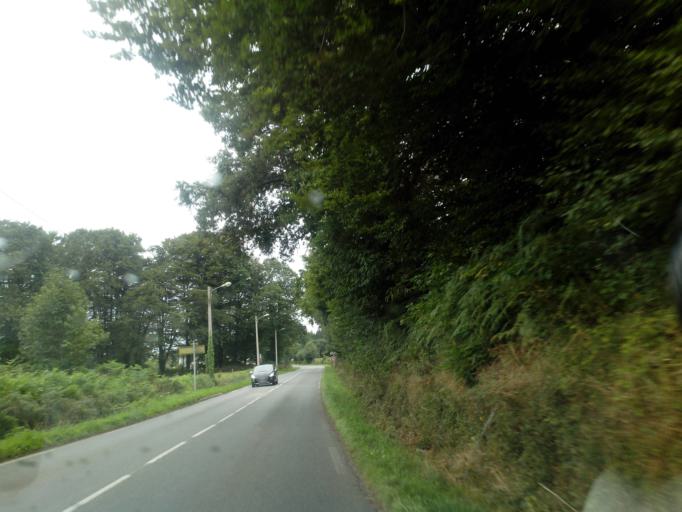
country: FR
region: Brittany
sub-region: Departement du Finistere
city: Tremeven
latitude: 47.8963
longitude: -3.5252
